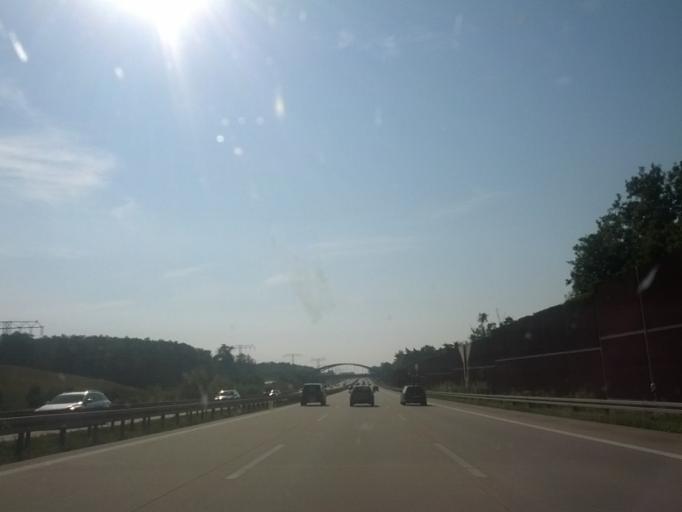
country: DE
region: Brandenburg
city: Neuenhagen
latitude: 52.5262
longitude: 13.7138
